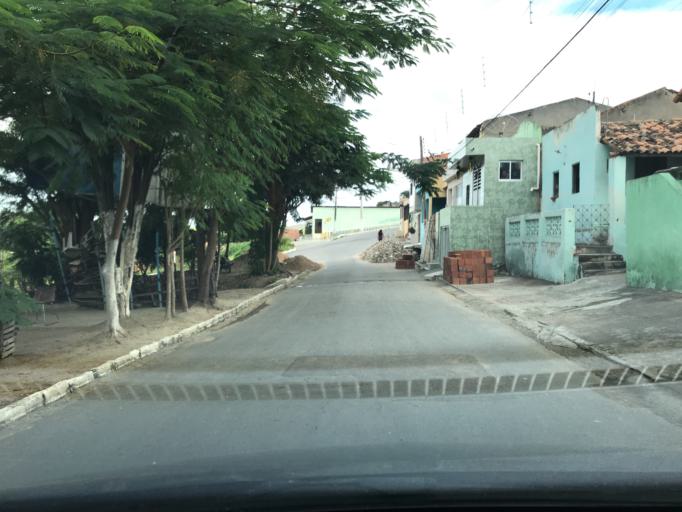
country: BR
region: Pernambuco
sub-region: Bezerros
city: Bezerros
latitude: -8.2337
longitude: -35.7562
